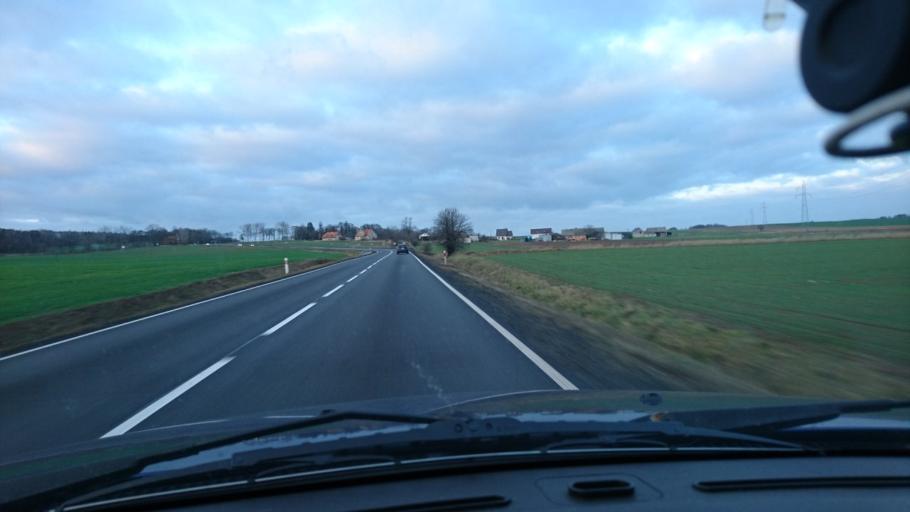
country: PL
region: Greater Poland Voivodeship
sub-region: Powiat ostrzeszowski
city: Ostrzeszow
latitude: 51.3637
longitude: 17.9460
